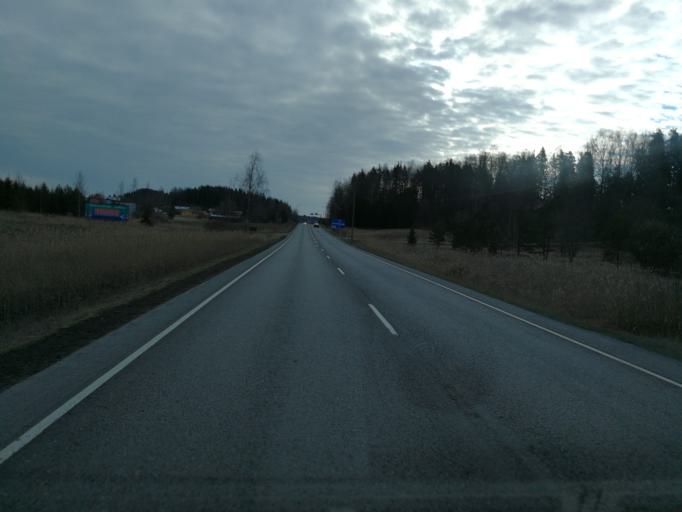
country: FI
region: Varsinais-Suomi
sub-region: Salo
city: Halikko
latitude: 60.3816
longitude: 23.0341
